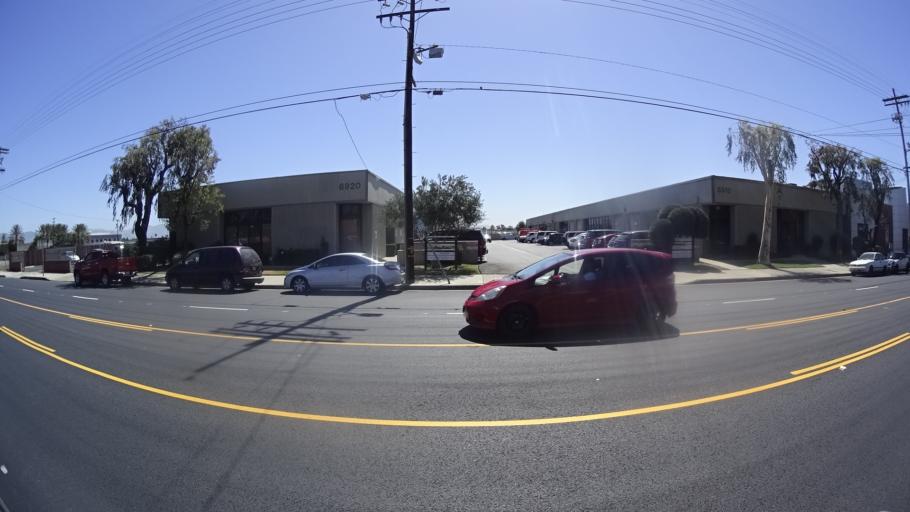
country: US
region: California
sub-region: Los Angeles County
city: Van Nuys
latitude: 34.1962
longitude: -118.4925
